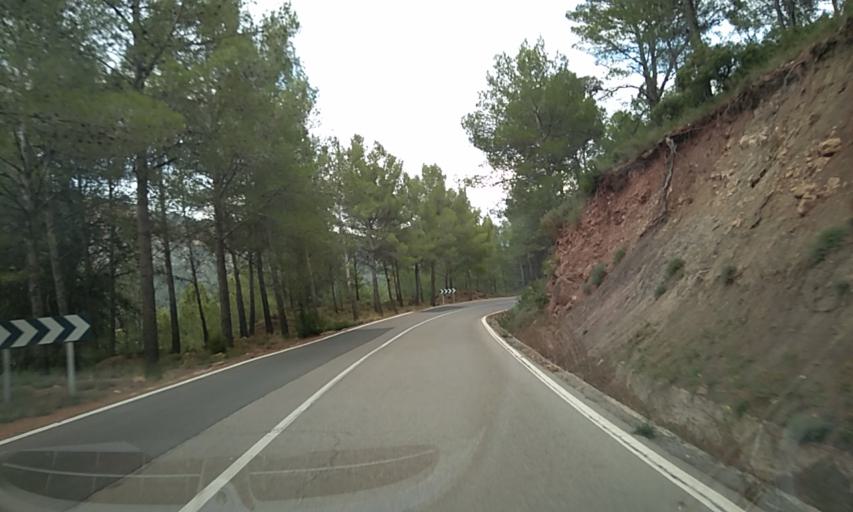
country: ES
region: Valencia
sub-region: Provincia de Castello
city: Puebla de Arenoso
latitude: 40.0880
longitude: -0.5590
